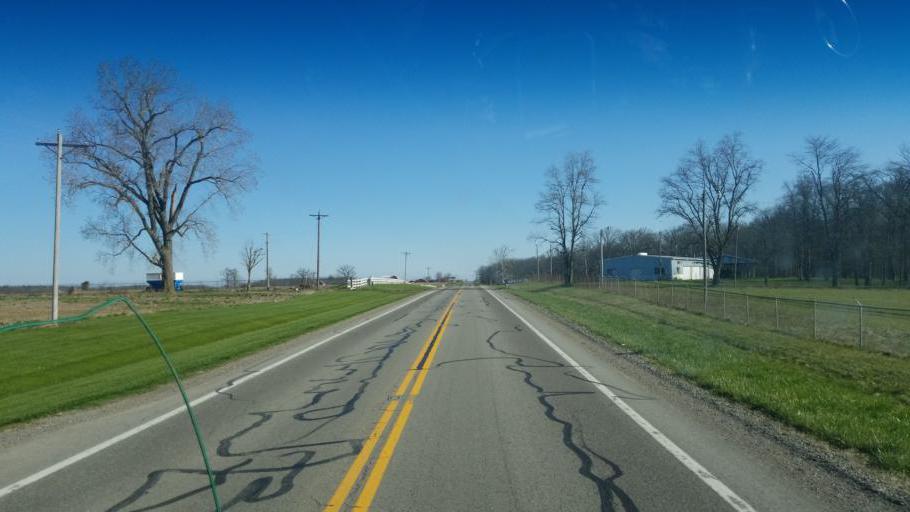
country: US
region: Ohio
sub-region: Hardin County
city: Kenton
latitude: 40.5623
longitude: -83.5885
